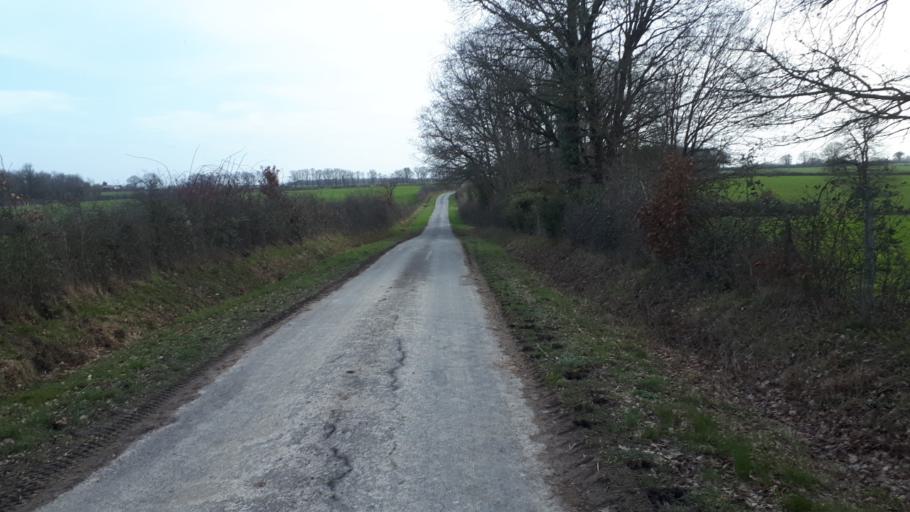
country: FR
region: Poitou-Charentes
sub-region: Departement de la Vienne
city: Archigny
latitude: 46.6245
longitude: 0.7456
